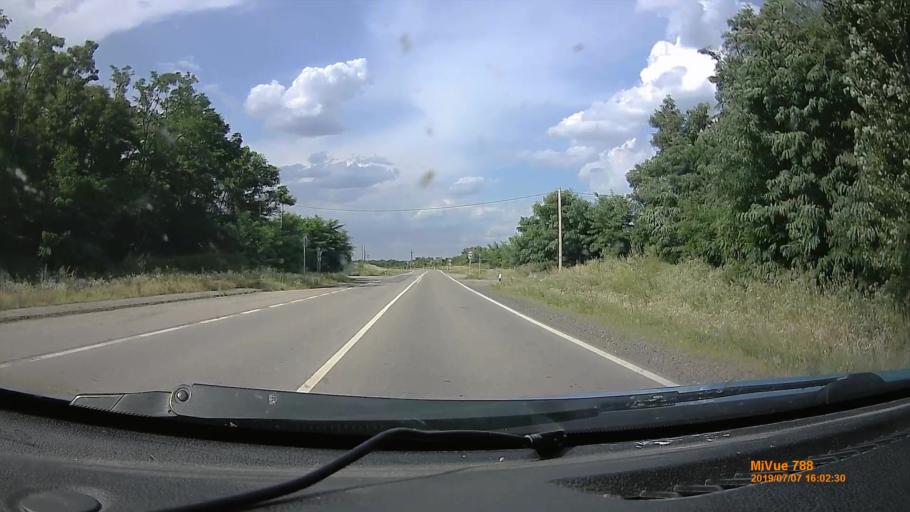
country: HU
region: Heves
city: Boldog
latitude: 47.6249
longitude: 19.7310
